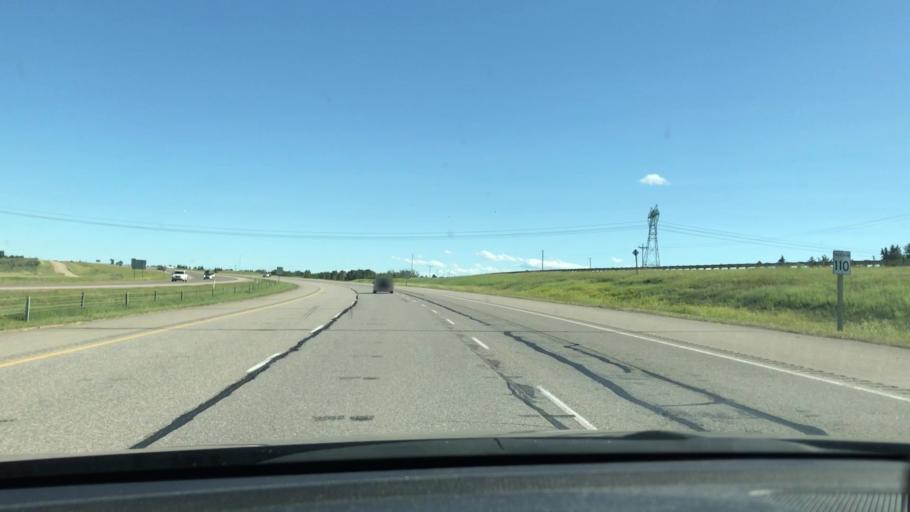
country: CA
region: Alberta
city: Crossfield
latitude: 51.4647
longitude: -114.0252
